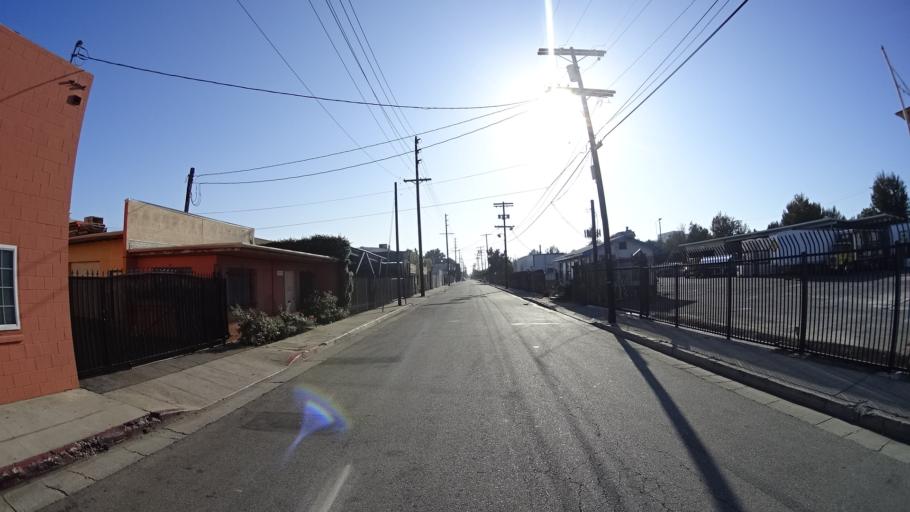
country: US
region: California
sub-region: Los Angeles County
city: Van Nuys
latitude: 34.1802
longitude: -118.4404
